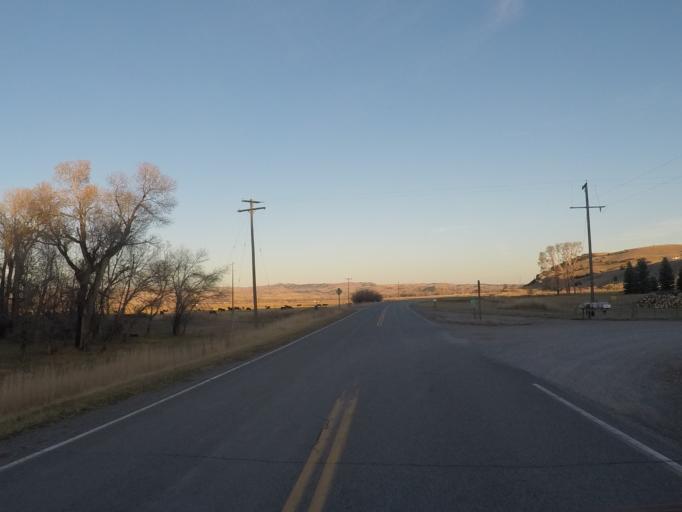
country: US
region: Montana
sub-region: Sweet Grass County
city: Big Timber
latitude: 45.7842
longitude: -109.8370
